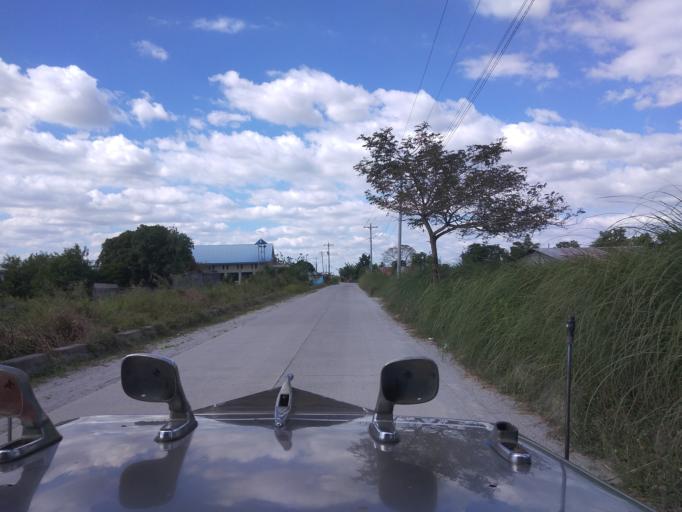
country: PH
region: Central Luzon
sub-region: Province of Pampanga
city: Magliman
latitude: 15.0424
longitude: 120.6297
